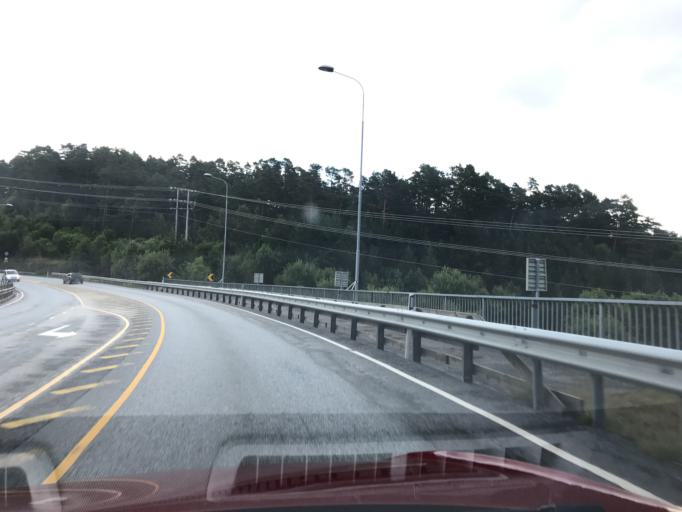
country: NO
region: Hordaland
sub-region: Stord
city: Leirvik
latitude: 59.7914
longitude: 5.4952
